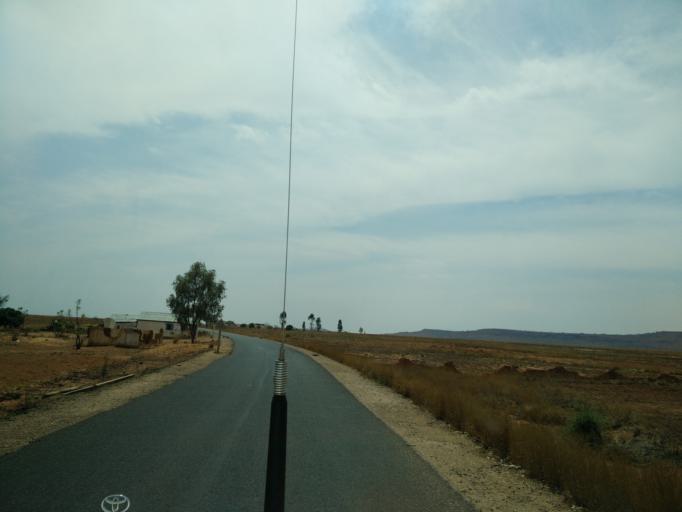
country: MG
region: Ihorombe
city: Ranohira
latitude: -22.7722
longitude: 45.1143
